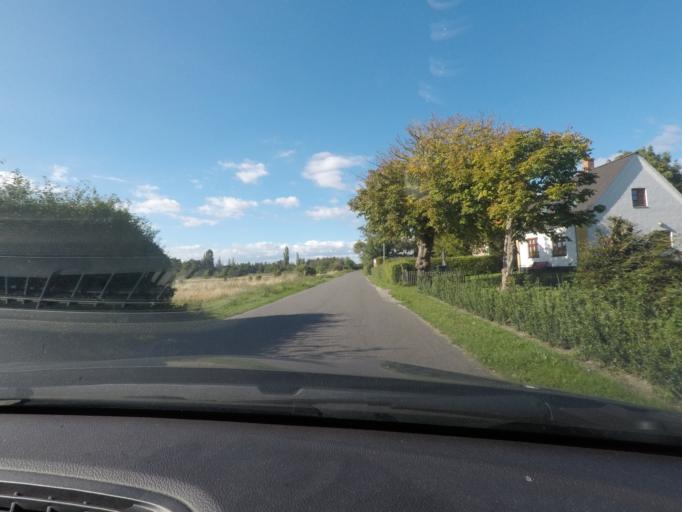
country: DK
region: Zealand
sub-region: Lolland Kommune
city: Maribo
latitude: 54.9744
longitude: 11.5134
